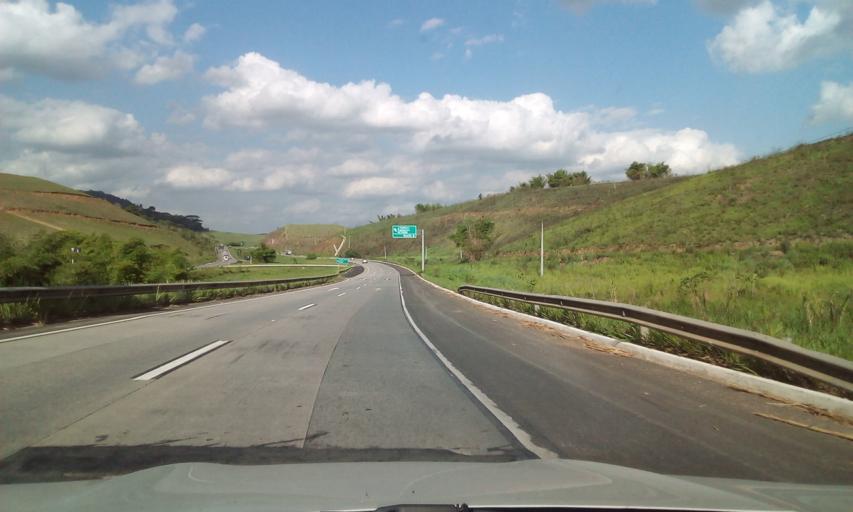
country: BR
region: Pernambuco
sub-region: Joaquim Nabuco
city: Joaquim Nabuco
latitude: -8.6096
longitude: -35.5448
